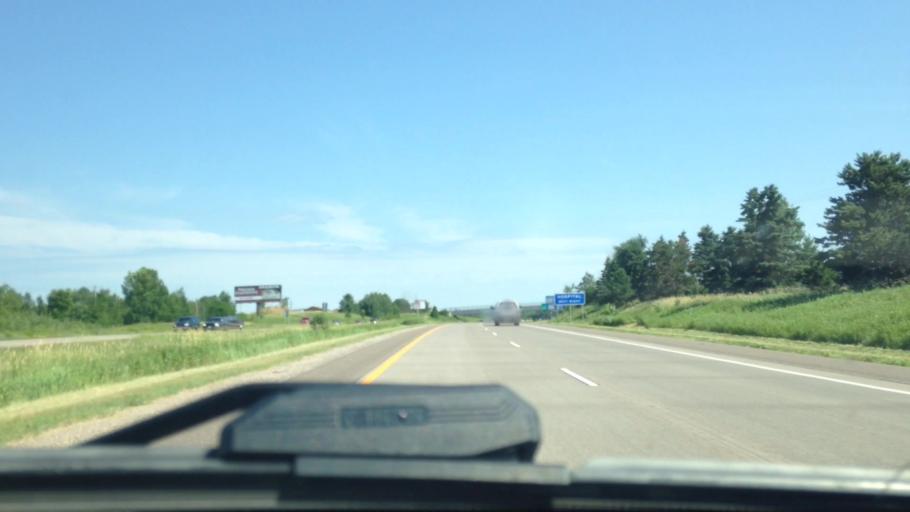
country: US
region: Wisconsin
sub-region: Barron County
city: Rice Lake
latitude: 45.4973
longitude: -91.7642
